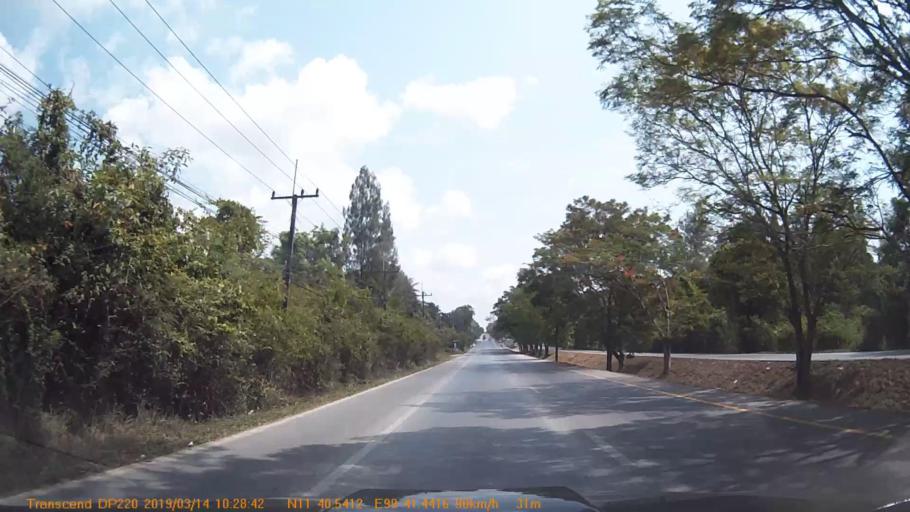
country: TH
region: Prachuap Khiri Khan
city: Thap Sakae
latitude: 11.6676
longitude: 99.6850
